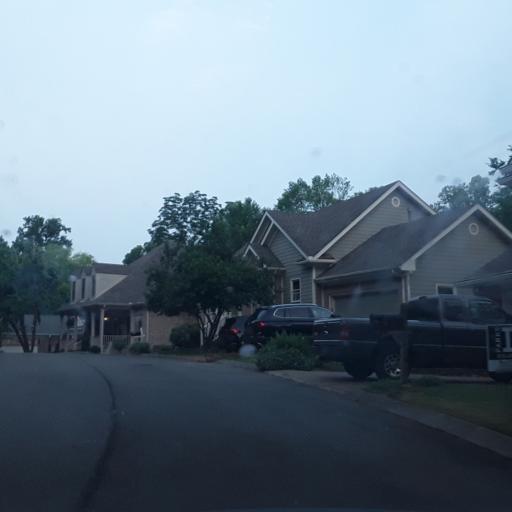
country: US
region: Tennessee
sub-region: Williamson County
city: Brentwood
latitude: 36.0481
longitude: -86.7652
